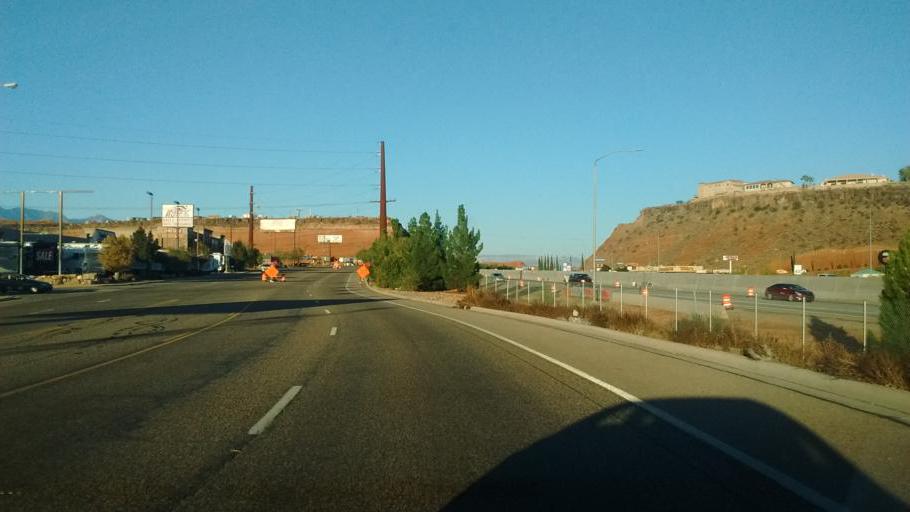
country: US
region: Utah
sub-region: Washington County
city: Saint George
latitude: 37.1132
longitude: -113.5567
